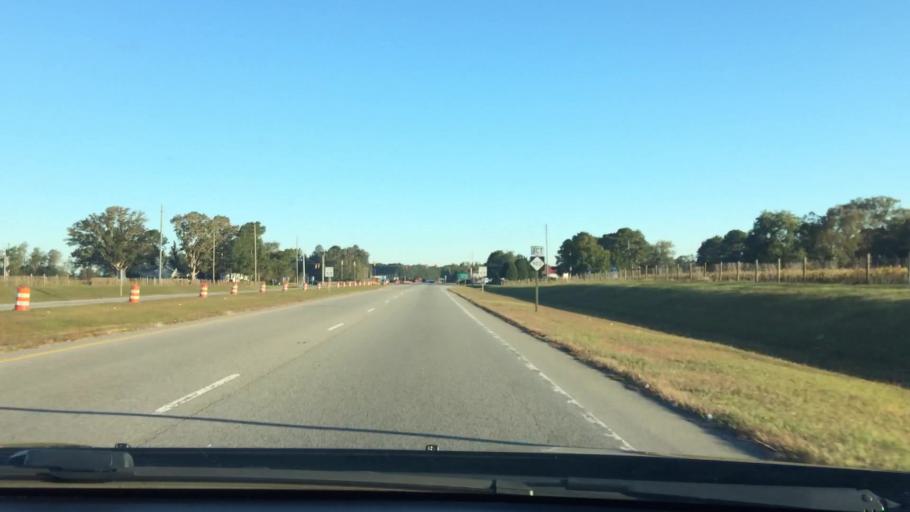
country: US
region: North Carolina
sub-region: Pitt County
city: Winterville
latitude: 35.5257
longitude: -77.4082
